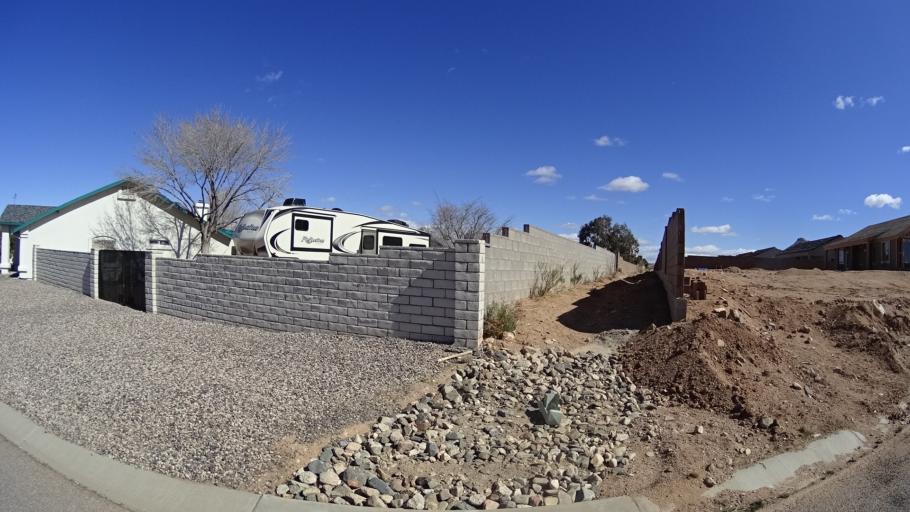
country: US
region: Arizona
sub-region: Mohave County
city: Kingman
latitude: 35.1970
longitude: -113.9657
